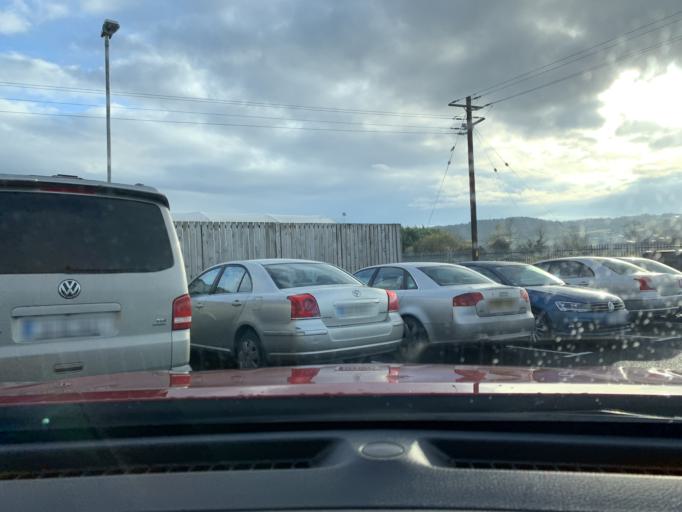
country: IE
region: Ulster
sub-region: County Donegal
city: Ballybofey
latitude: 54.8017
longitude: -7.7694
